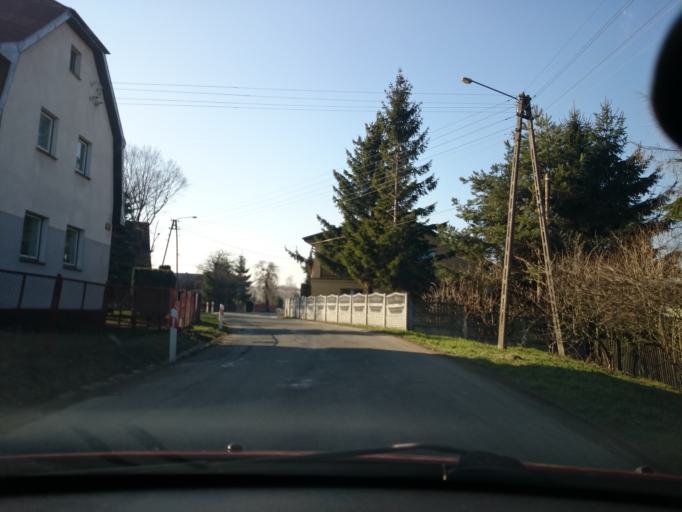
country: PL
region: Lower Silesian Voivodeship
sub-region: Powiat klodzki
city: Klodzko
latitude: 50.3818
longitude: 16.6335
